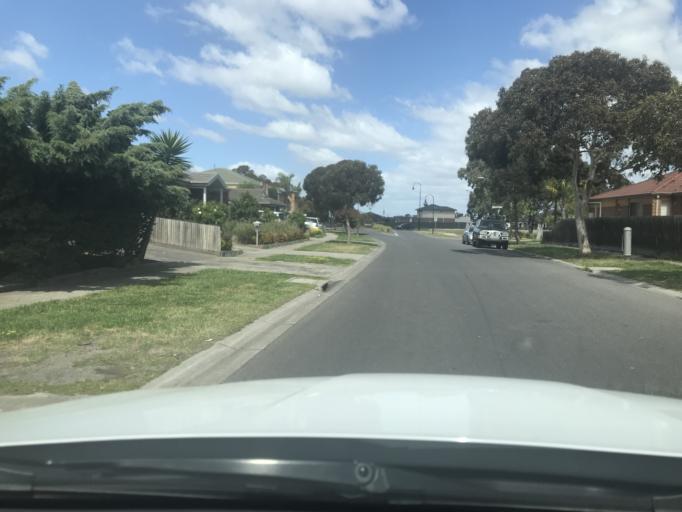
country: AU
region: Victoria
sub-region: Hume
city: Roxburgh Park
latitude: -37.6187
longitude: 144.9323
